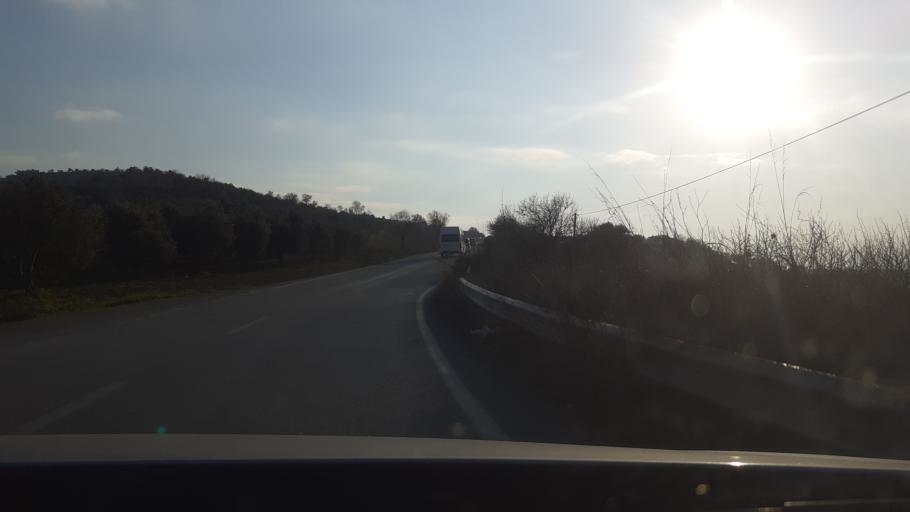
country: TR
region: Hatay
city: Oymakli
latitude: 36.1255
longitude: 36.3097
